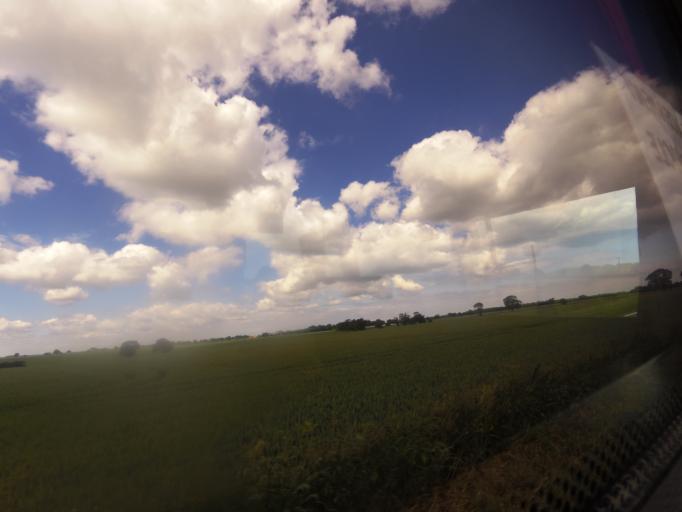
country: GB
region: England
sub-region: Norfolk
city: Aylsham
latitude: 52.8477
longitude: 1.2804
